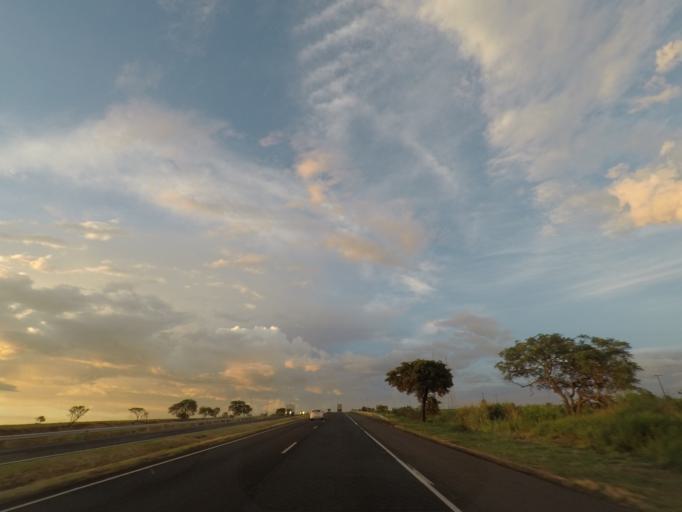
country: BR
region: Minas Gerais
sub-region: Uberaba
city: Uberaba
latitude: -19.6542
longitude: -48.0045
